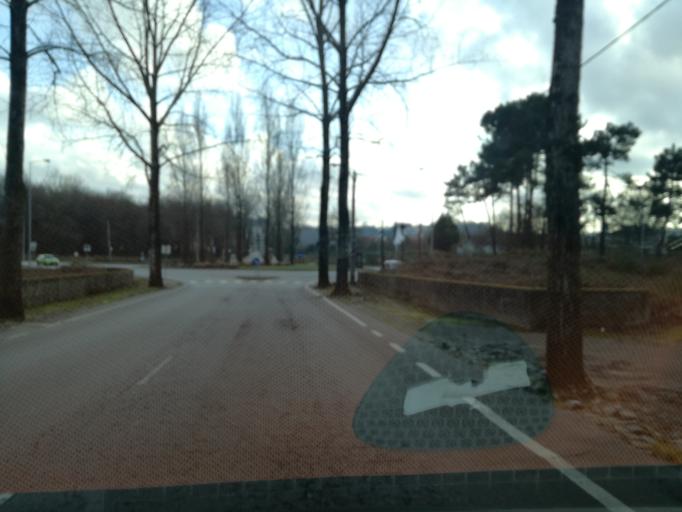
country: PT
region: Porto
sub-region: Maia
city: Nogueira
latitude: 41.2598
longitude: -8.5998
